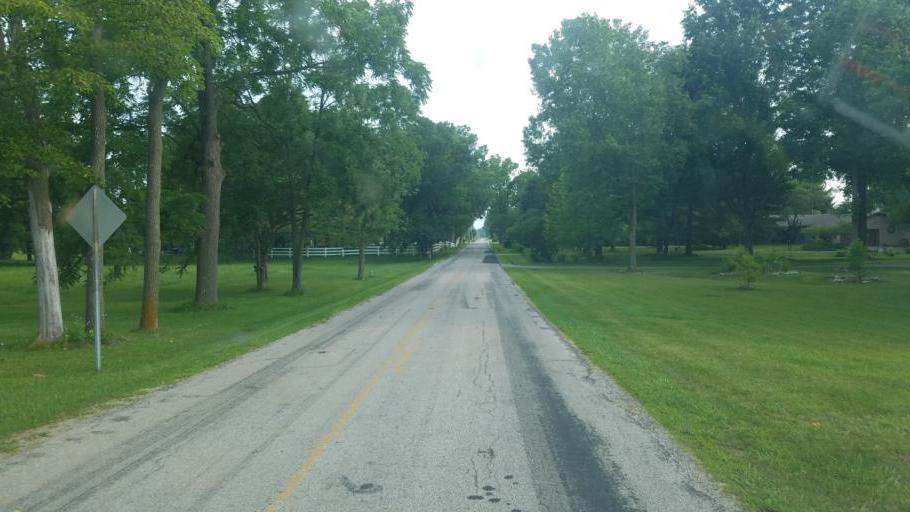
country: US
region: Ohio
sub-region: Marion County
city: Marion
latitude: 40.4981
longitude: -83.0535
